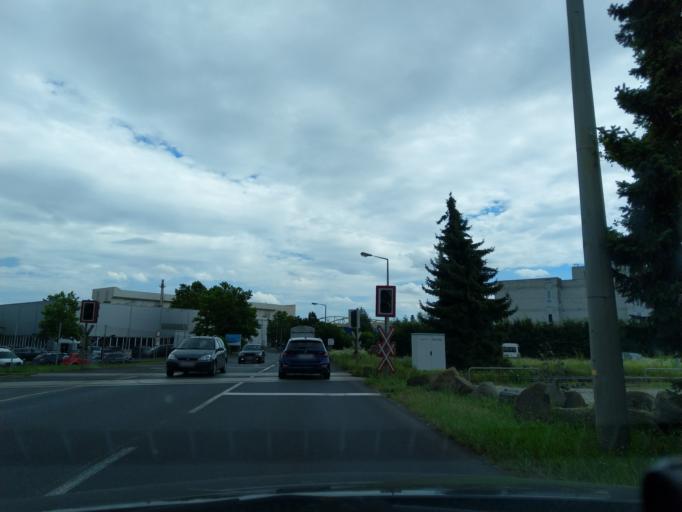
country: AT
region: Upper Austria
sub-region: Politischer Bezirk Urfahr-Umgebung
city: Steyregg
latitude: 48.2670
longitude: 14.3278
